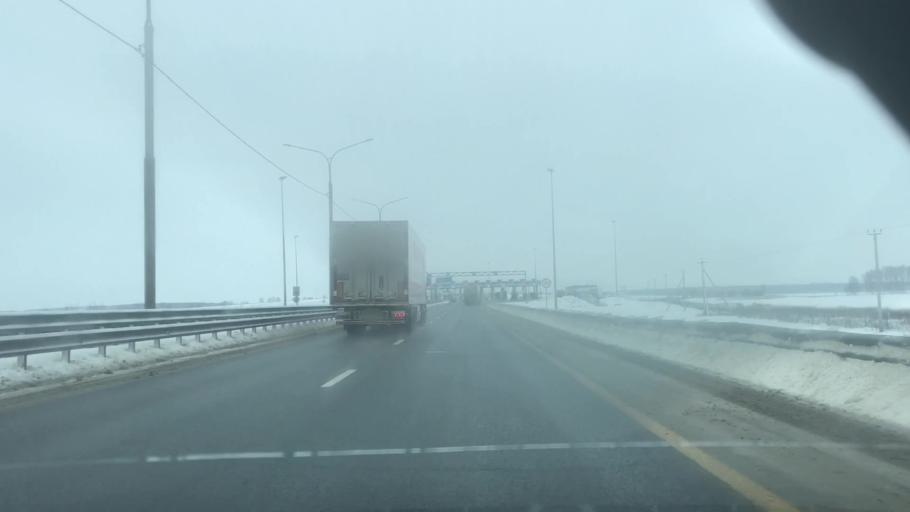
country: RU
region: Tula
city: Dubovka
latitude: 53.8816
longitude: 38.0501
